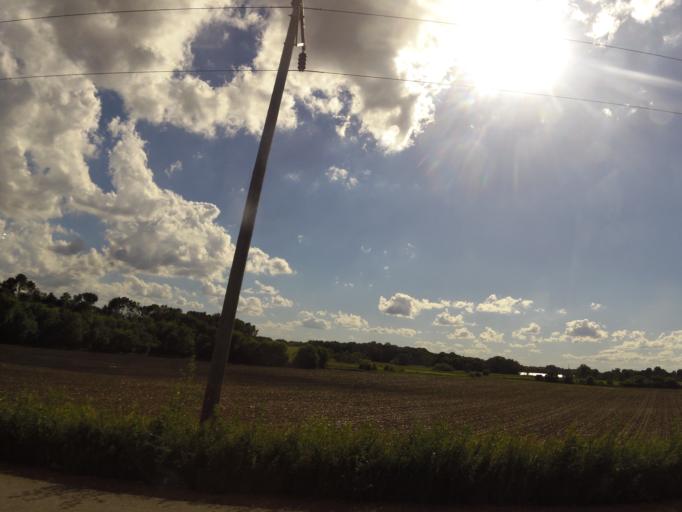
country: US
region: Minnesota
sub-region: Carver County
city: Waconia
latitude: 44.8857
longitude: -93.8172
